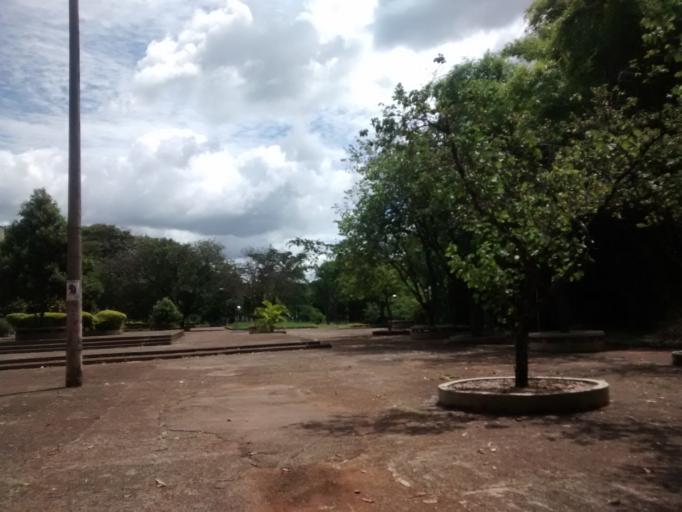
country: BR
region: Federal District
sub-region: Brasilia
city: Brasilia
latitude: -15.7644
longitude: -47.8698
